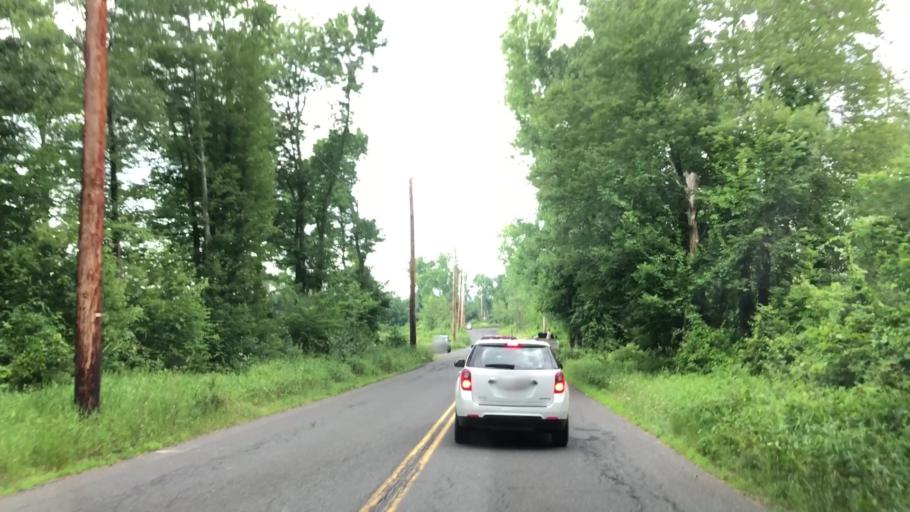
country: US
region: Massachusetts
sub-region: Hampshire County
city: Southampton
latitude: 42.1817
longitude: -72.7499
